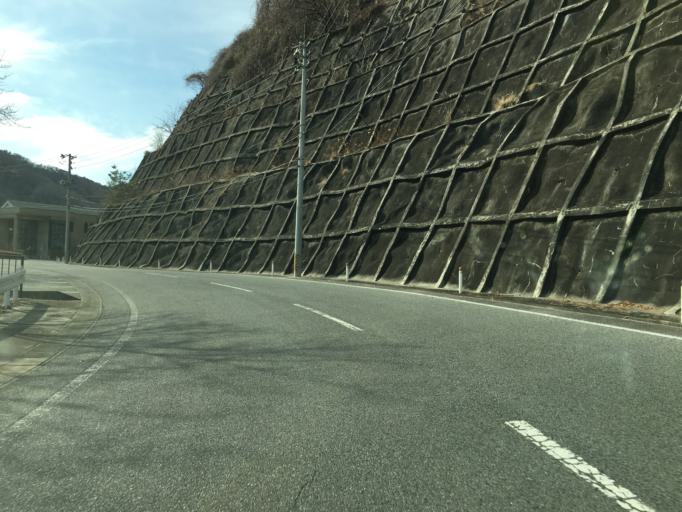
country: JP
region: Fukushima
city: Iwaki
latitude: 37.1259
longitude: 140.8284
